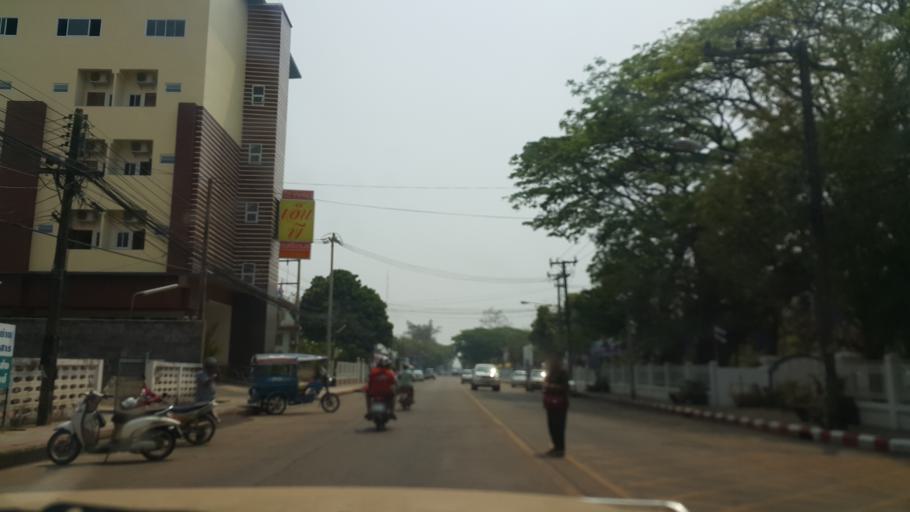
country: TH
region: Nakhon Phanom
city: Nakhon Phanom
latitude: 17.4104
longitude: 104.7799
